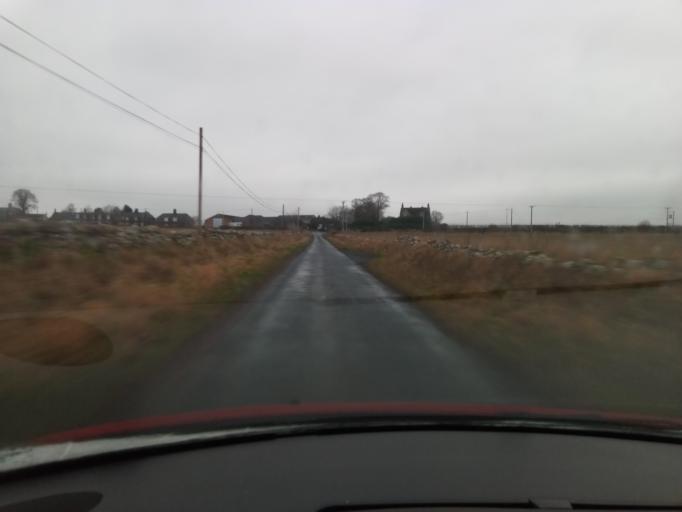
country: GB
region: Scotland
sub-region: The Scottish Borders
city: Kelso
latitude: 55.5714
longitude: -2.4527
